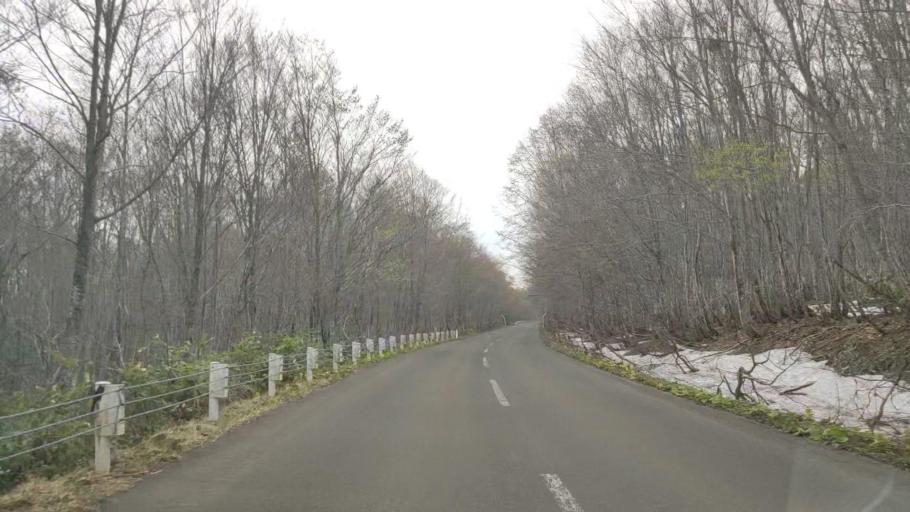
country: JP
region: Aomori
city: Aomori Shi
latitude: 40.6622
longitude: 140.9605
